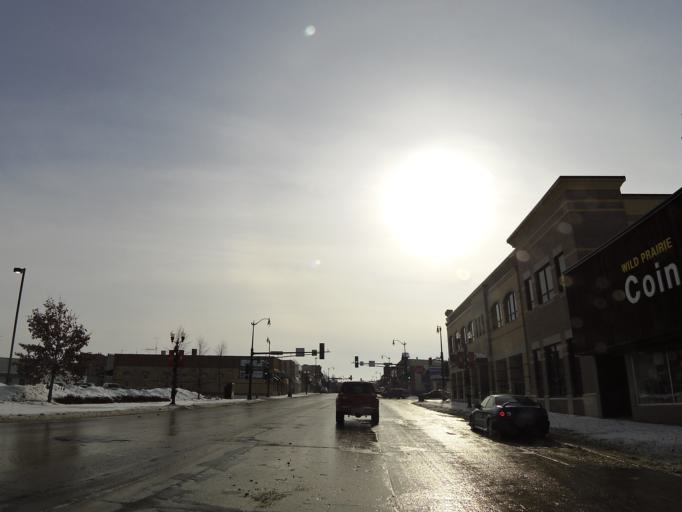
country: US
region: Minnesota
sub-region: McLeod County
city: Hutchinson
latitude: 44.8941
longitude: -94.3694
